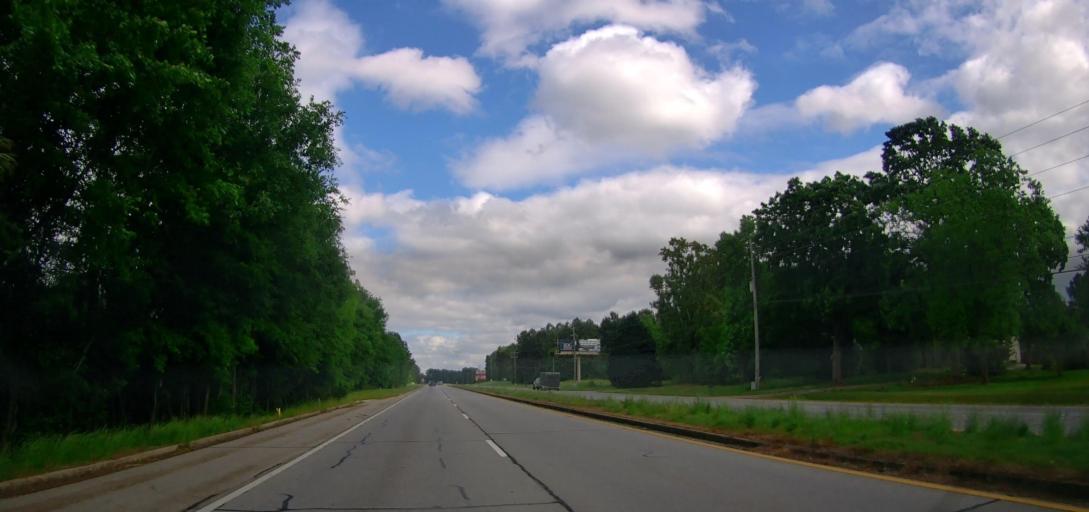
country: US
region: Georgia
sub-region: Walton County
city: Walnut Grove
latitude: 33.8149
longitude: -83.8040
